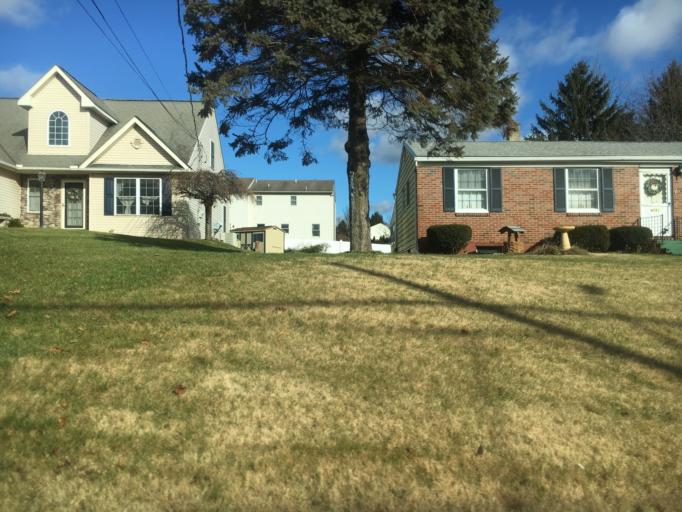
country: US
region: Pennsylvania
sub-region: Lehigh County
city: Egypt
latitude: 40.6812
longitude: -75.5378
